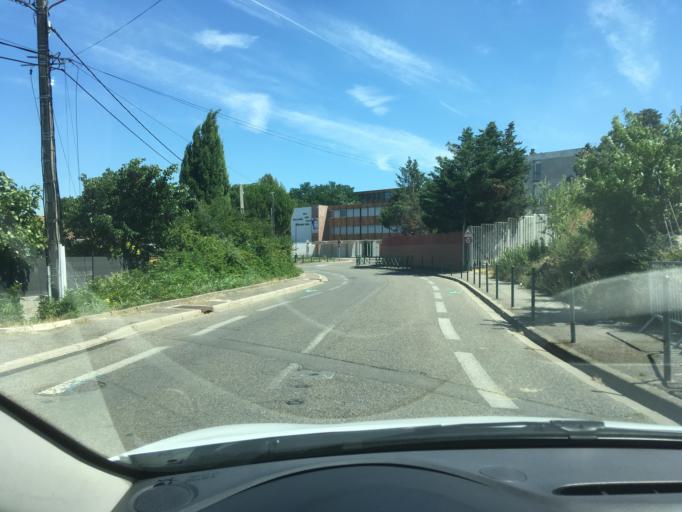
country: FR
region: Provence-Alpes-Cote d'Azur
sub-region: Departement des Bouches-du-Rhone
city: Chateaurenard
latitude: 43.8825
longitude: 4.8635
